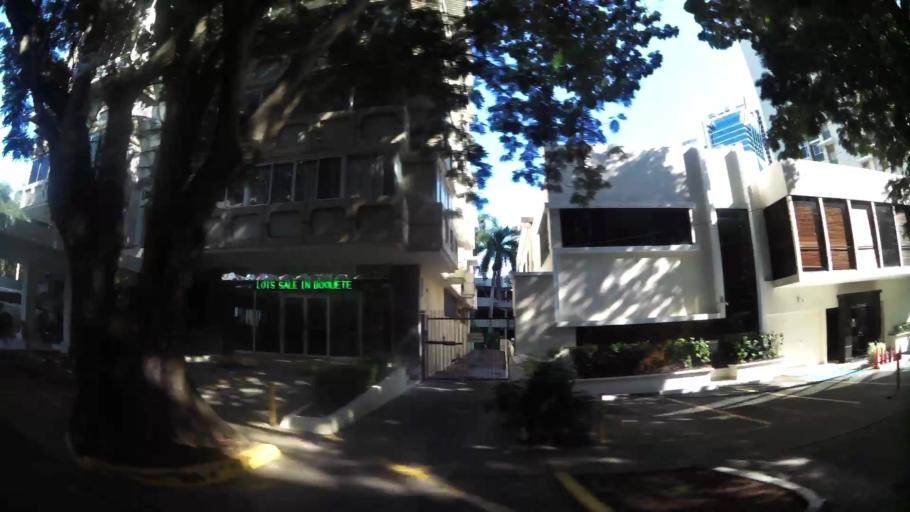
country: PA
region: Panama
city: Panama
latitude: 8.9829
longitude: -79.5230
